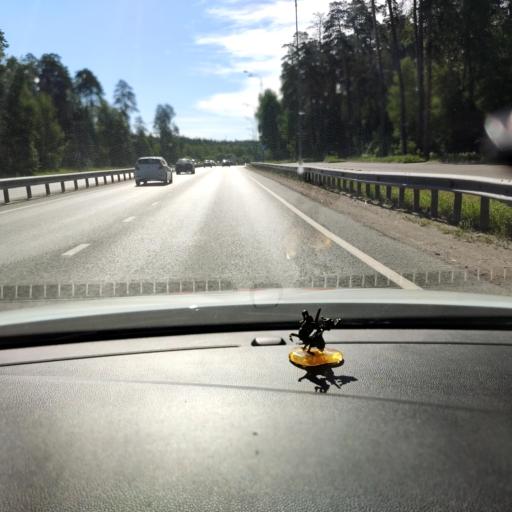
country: RU
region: Tatarstan
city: Staroye Arakchino
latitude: 55.8351
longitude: 48.9744
